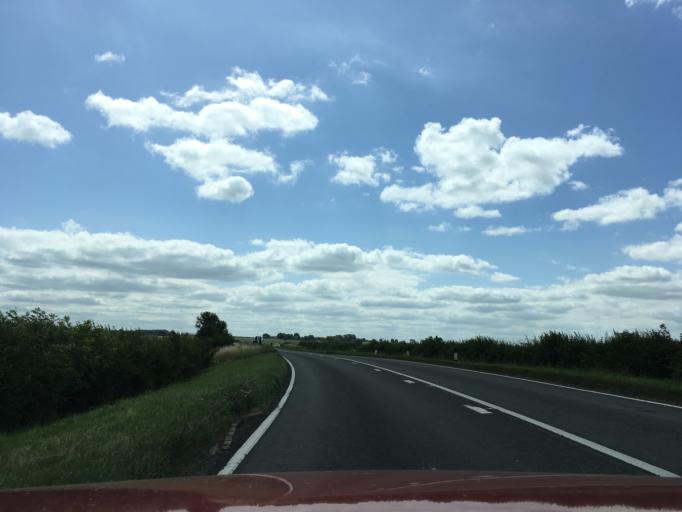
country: GB
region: England
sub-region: Buckinghamshire
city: Winslow
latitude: 51.9086
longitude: -0.8379
